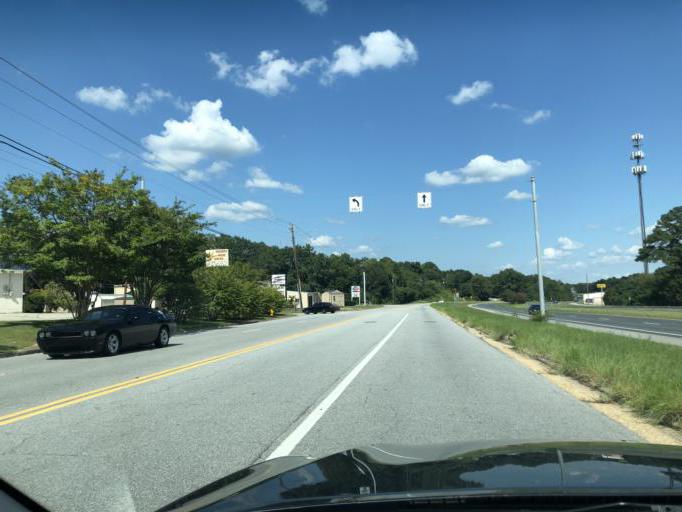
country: US
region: Georgia
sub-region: Muscogee County
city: Columbus
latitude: 32.5131
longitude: -84.9271
